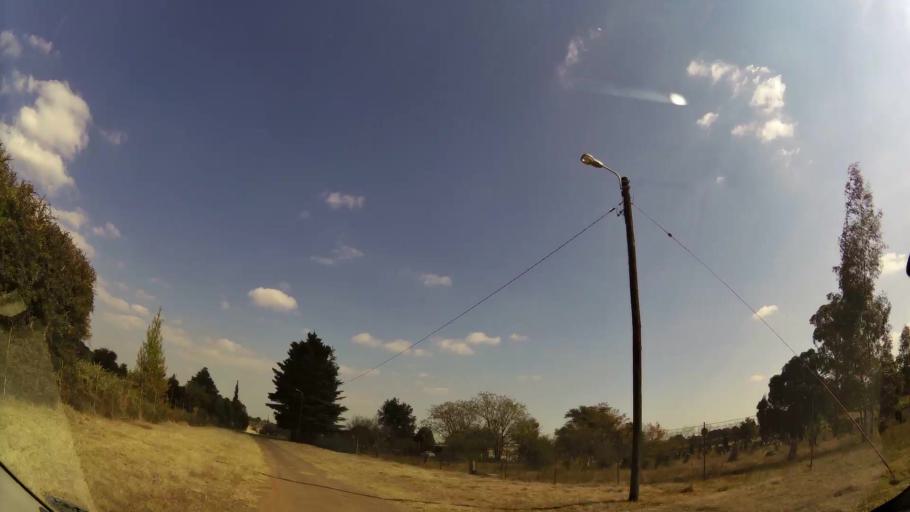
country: ZA
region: Gauteng
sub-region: Ekurhuleni Metropolitan Municipality
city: Benoni
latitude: -26.0768
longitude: 28.3426
